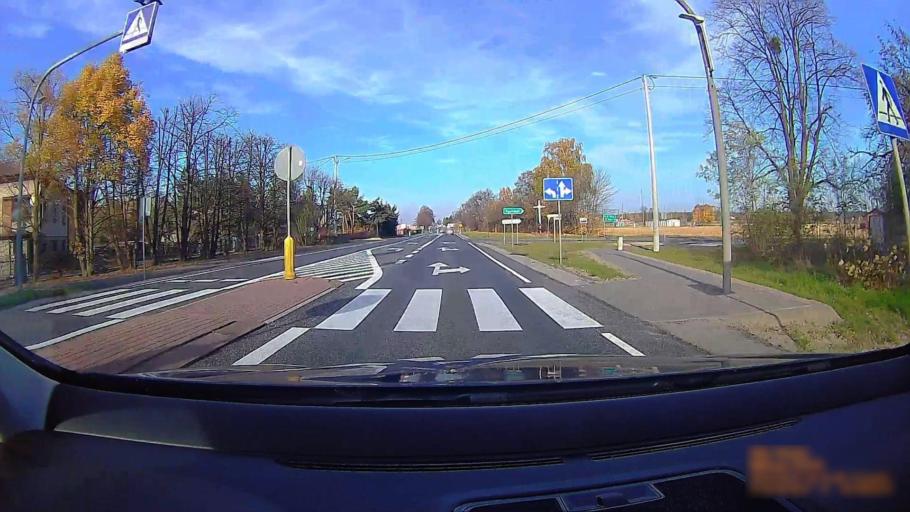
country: PL
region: Greater Poland Voivodeship
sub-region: Powiat koninski
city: Rychwal
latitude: 52.0776
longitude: 18.1600
